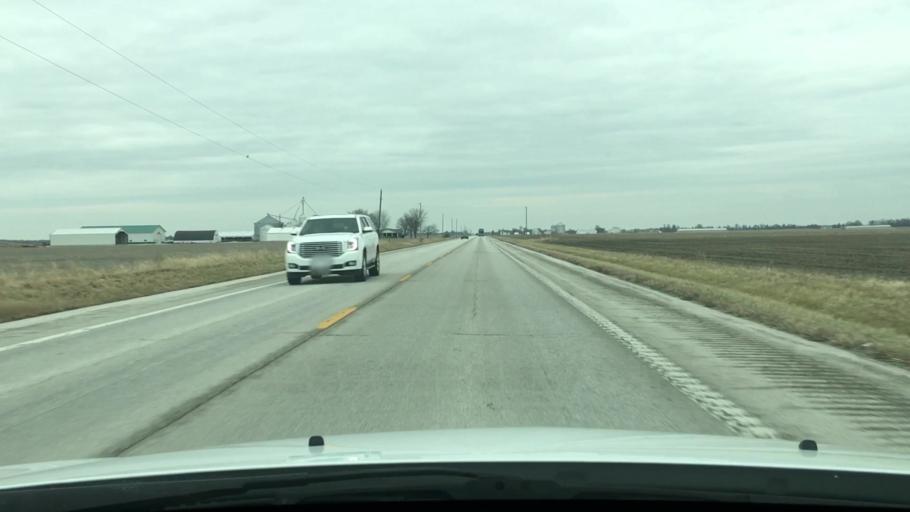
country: US
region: Missouri
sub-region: Audrain County
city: Vandalia
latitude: 39.2665
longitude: -91.6447
